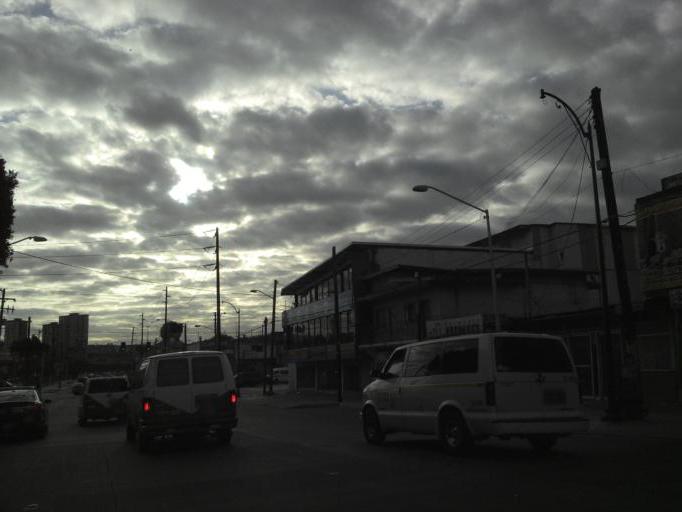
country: MX
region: Baja California
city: Tijuana
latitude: 32.5356
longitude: -117.0348
